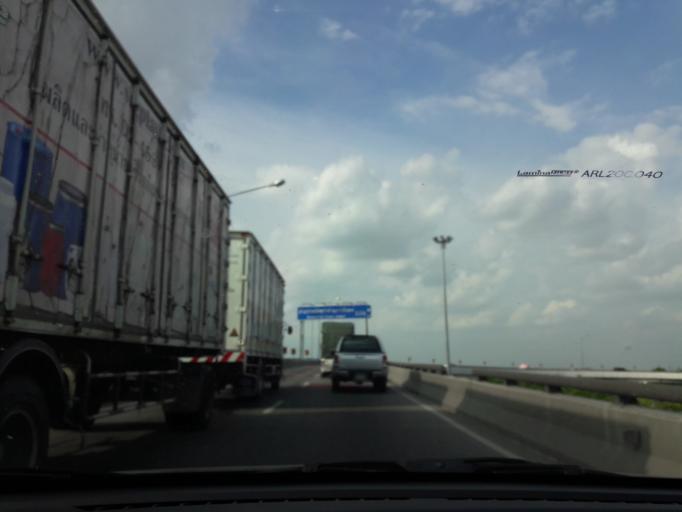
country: TH
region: Bangkok
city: Bang Bon
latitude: 13.6439
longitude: 100.4085
